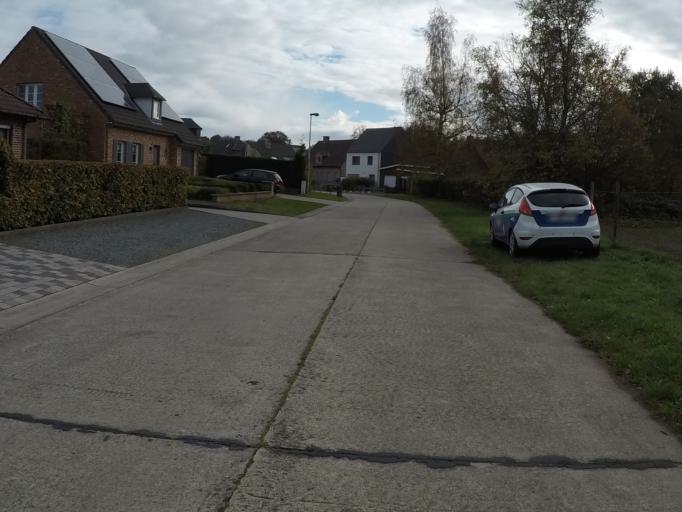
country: BE
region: Flanders
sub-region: Provincie Antwerpen
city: Nijlen
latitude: 51.1569
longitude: 4.6515
